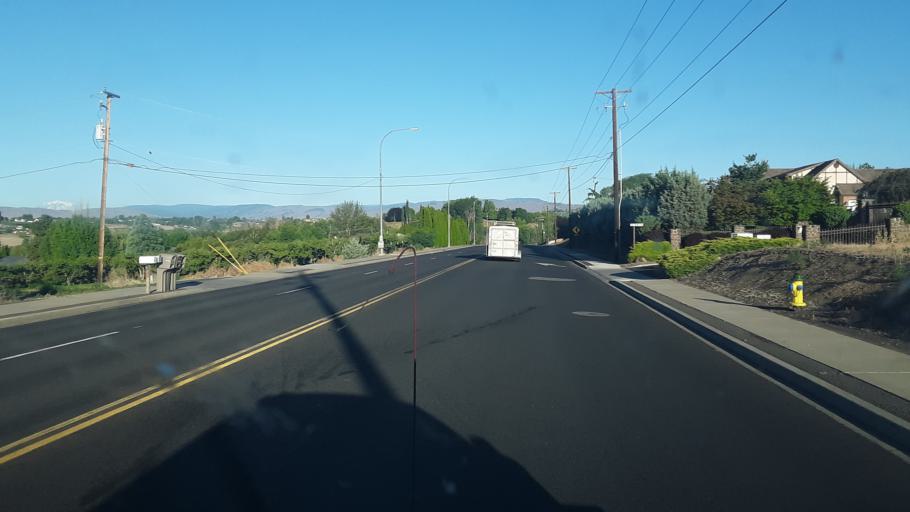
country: US
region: Washington
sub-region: Yakima County
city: West Valley
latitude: 46.6003
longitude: -120.6380
